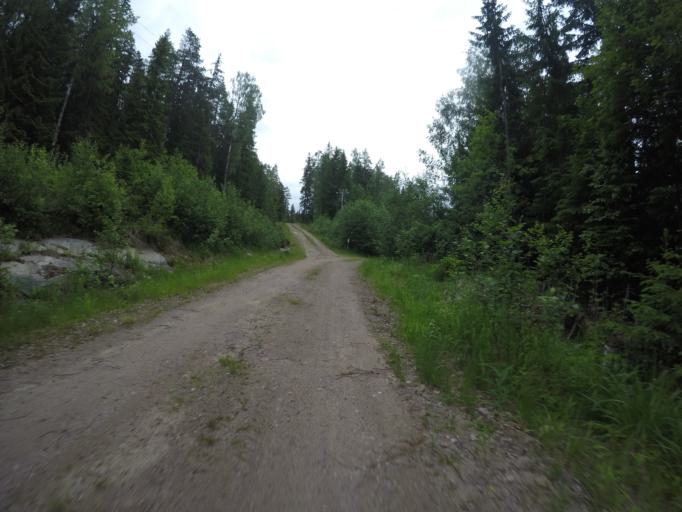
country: SE
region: Dalarna
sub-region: Ludvika Kommun
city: Abborrberget
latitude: 60.0684
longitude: 14.5638
